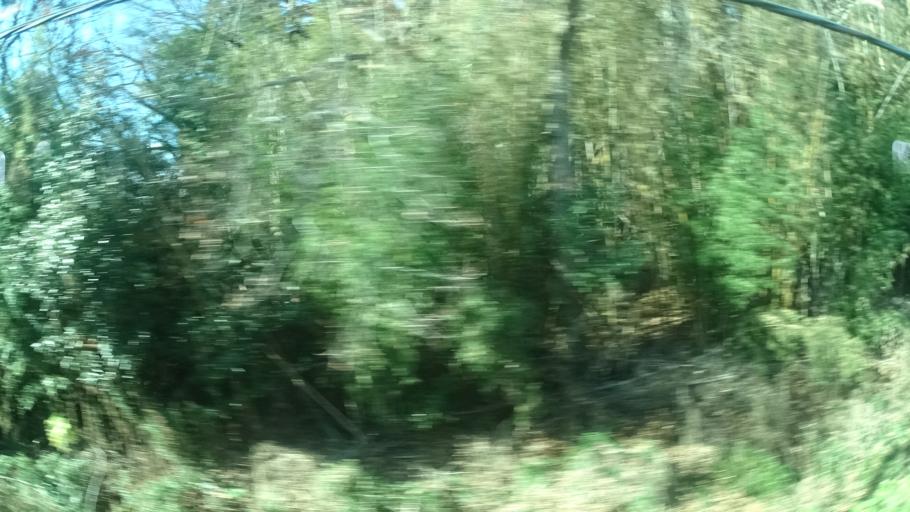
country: JP
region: Fukushima
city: Namie
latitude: 37.6619
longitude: 140.9693
